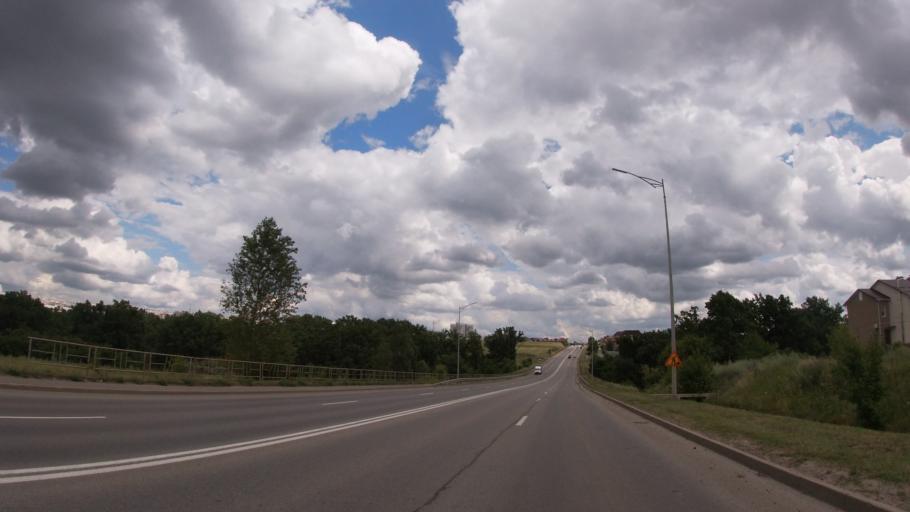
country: RU
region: Belgorod
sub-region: Belgorodskiy Rayon
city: Belgorod
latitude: 50.5506
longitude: 36.5495
